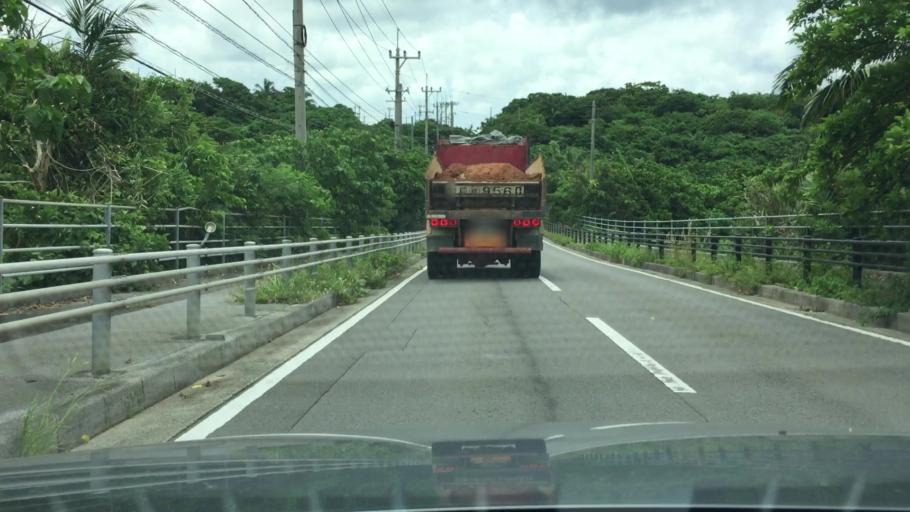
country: JP
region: Okinawa
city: Ishigaki
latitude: 24.4534
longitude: 124.2004
